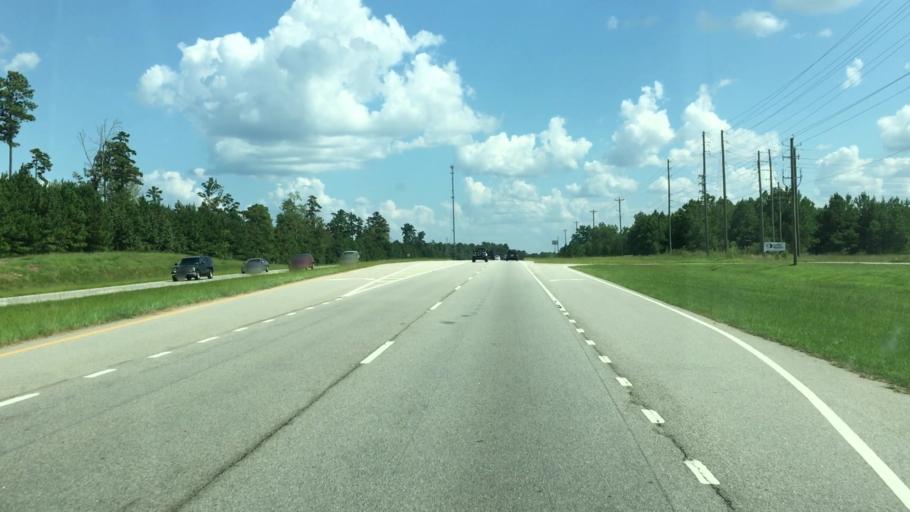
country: US
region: Georgia
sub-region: Putnam County
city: Eatonton
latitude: 33.2148
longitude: -83.3038
